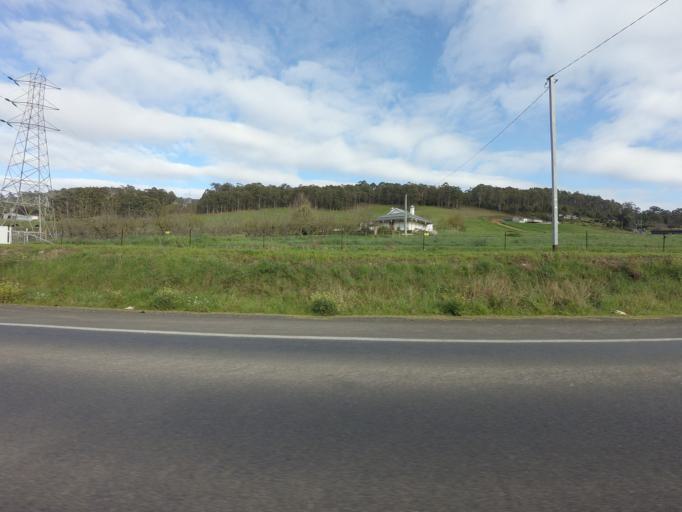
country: AU
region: Tasmania
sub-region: Huon Valley
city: Huonville
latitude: -43.0413
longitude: 147.0448
